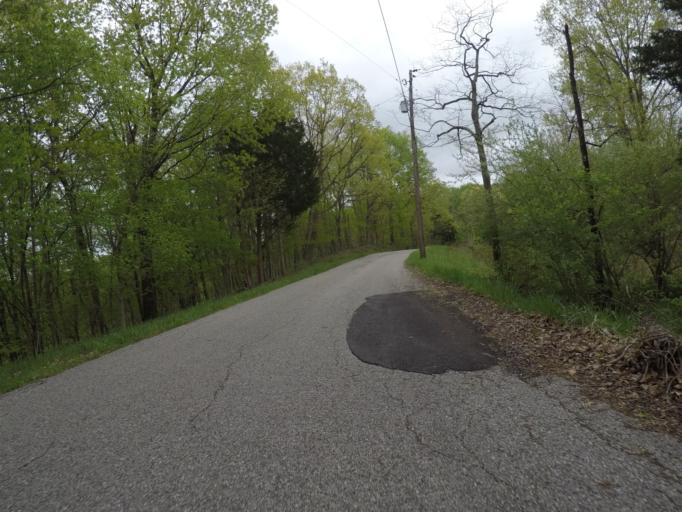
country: US
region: West Virginia
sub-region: Cabell County
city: Barboursville
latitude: 38.3976
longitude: -82.2533
